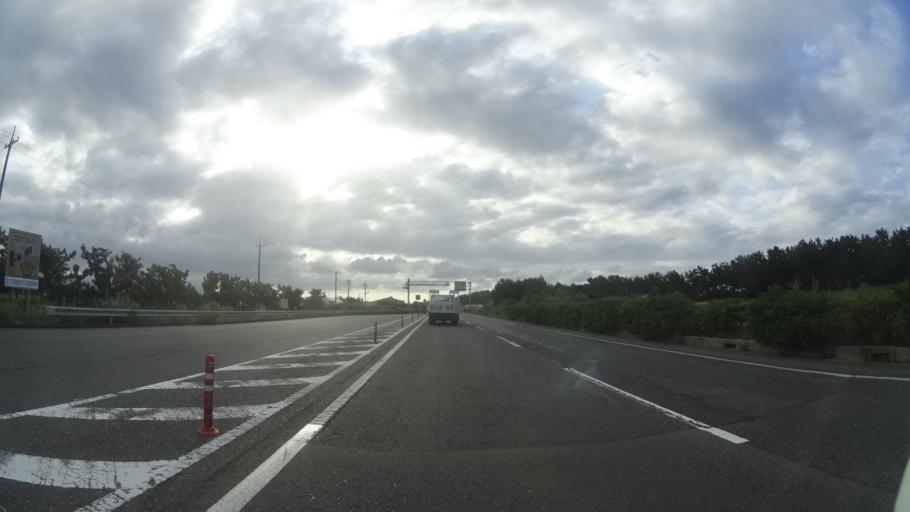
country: JP
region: Tottori
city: Kurayoshi
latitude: 35.4985
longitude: 133.7717
